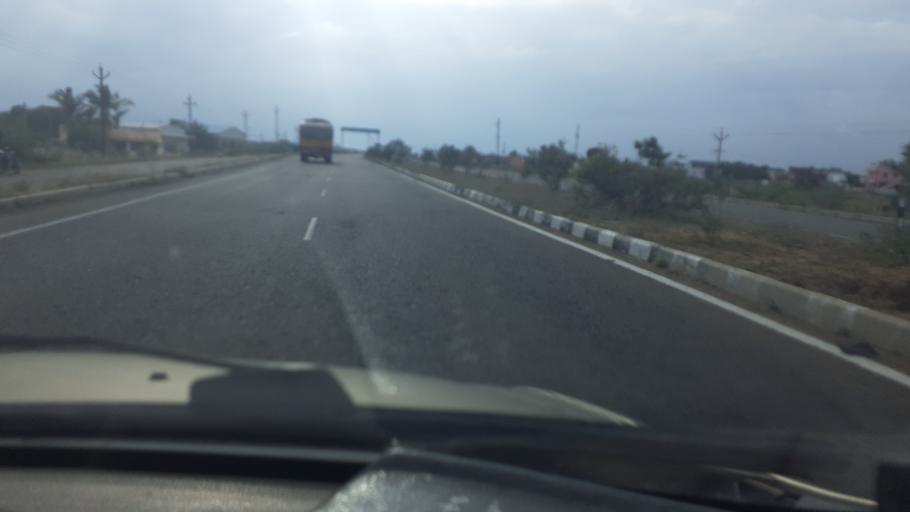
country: IN
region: Tamil Nadu
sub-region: Tirunelveli Kattabo
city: Tirunelveli
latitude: 8.6626
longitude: 77.7251
